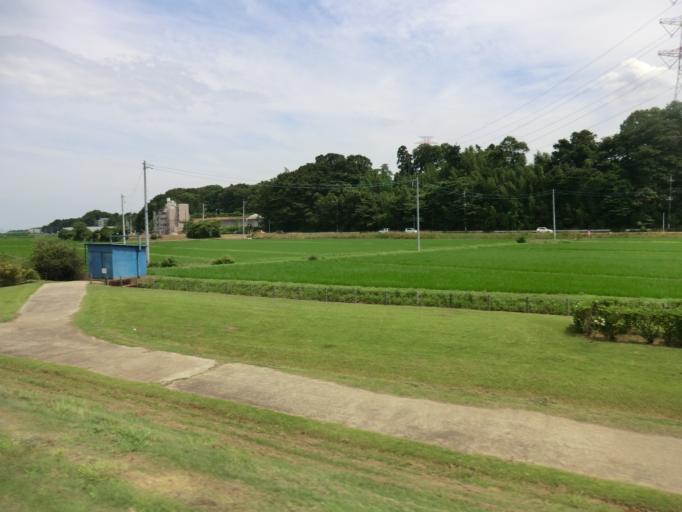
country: JP
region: Chiba
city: Abiko
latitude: 35.8587
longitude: 140.0083
